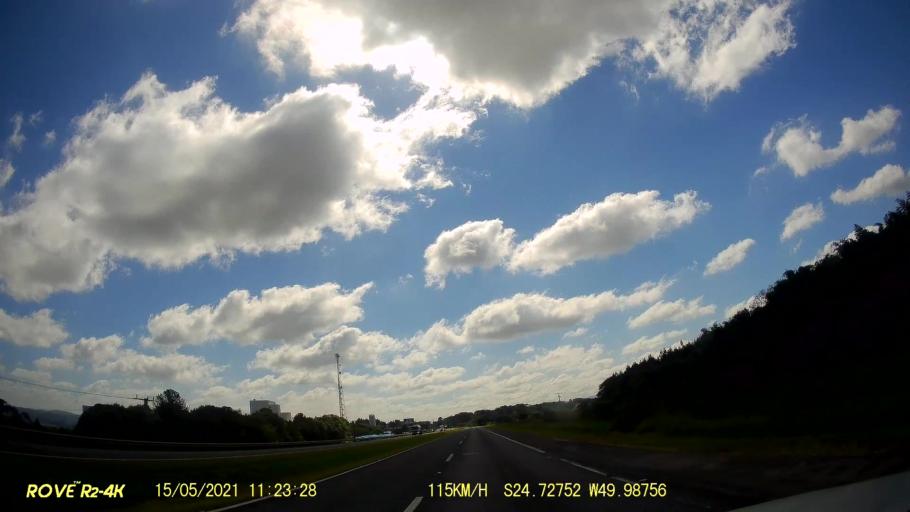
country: BR
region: Parana
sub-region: Castro
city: Castro
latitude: -24.7277
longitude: -49.9876
